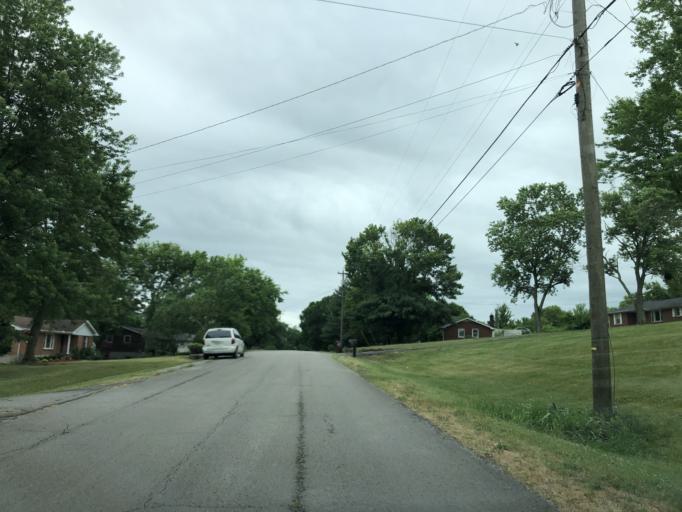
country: US
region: Tennessee
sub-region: Davidson County
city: Goodlettsville
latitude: 36.2727
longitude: -86.7658
